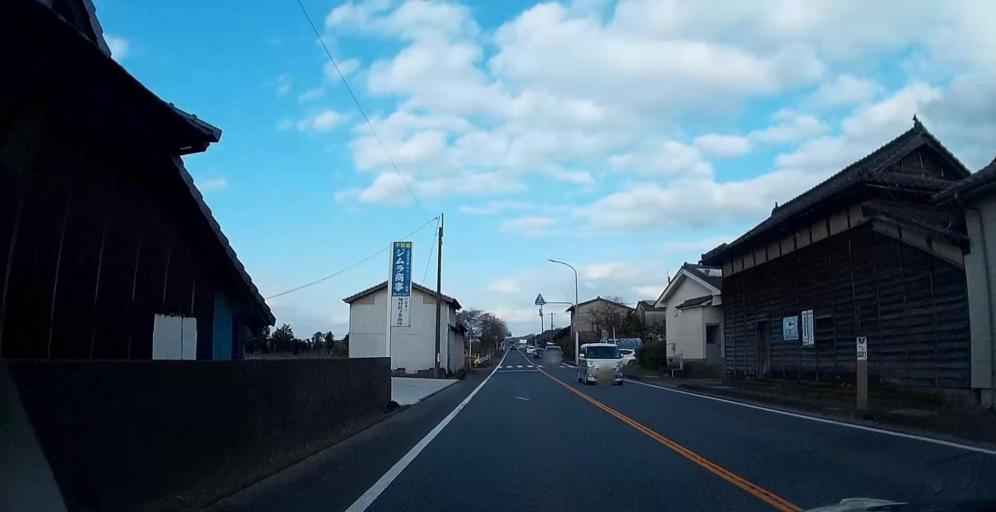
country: JP
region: Kumamoto
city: Yatsushiro
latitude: 32.5403
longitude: 130.6724
